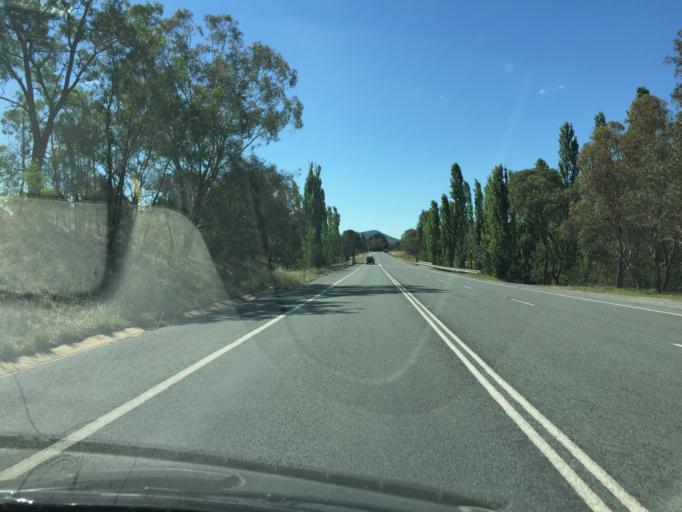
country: AU
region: Australian Capital Territory
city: Macarthur
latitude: -35.4419
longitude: 149.1292
